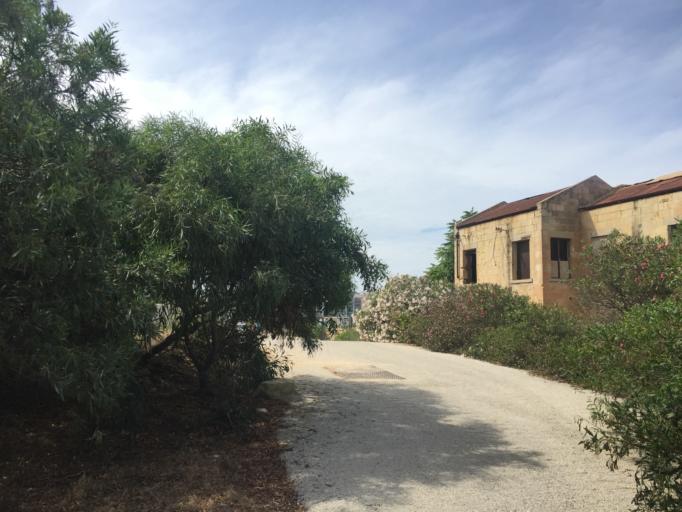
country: MT
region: Il-Furjana
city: Floriana
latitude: 35.9042
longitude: 14.5066
